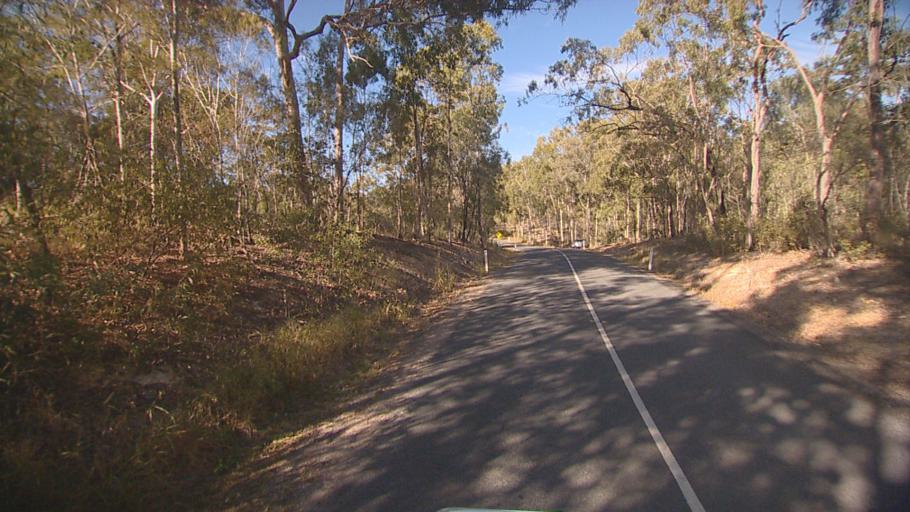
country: AU
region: Queensland
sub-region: Logan
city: Windaroo
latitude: -27.8168
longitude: 153.1687
